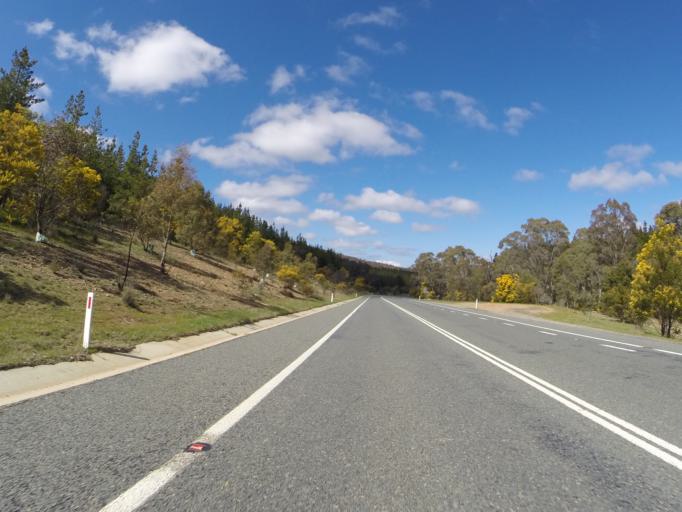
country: AU
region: New South Wales
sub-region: Queanbeyan
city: Queanbeyan
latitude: -35.2644
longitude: 149.2633
